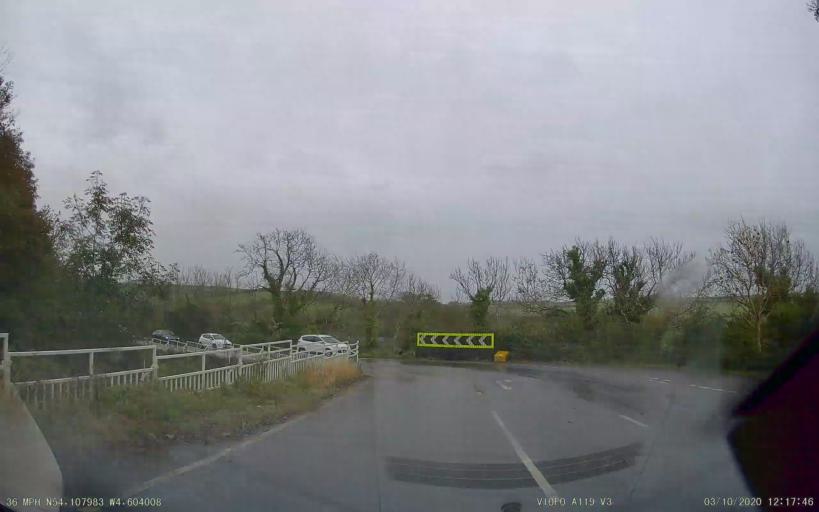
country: IM
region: Castletown
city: Castletown
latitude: 54.1080
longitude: -4.6040
